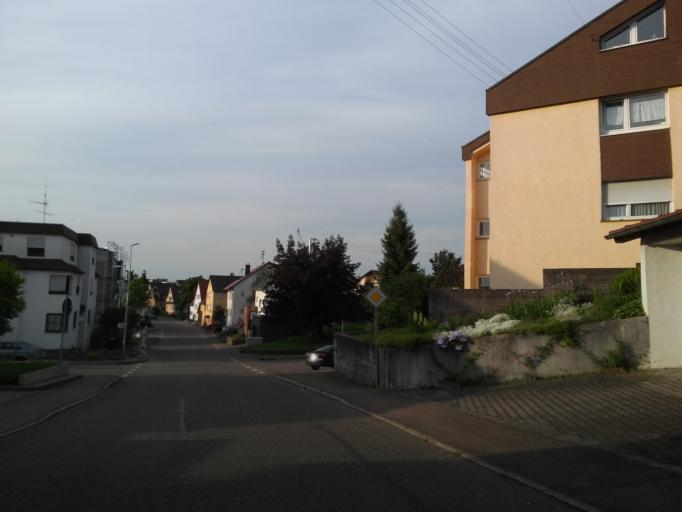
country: DE
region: Baden-Wuerttemberg
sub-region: Regierungsbezirk Stuttgart
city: Leutenbach
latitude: 48.9003
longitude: 9.4049
